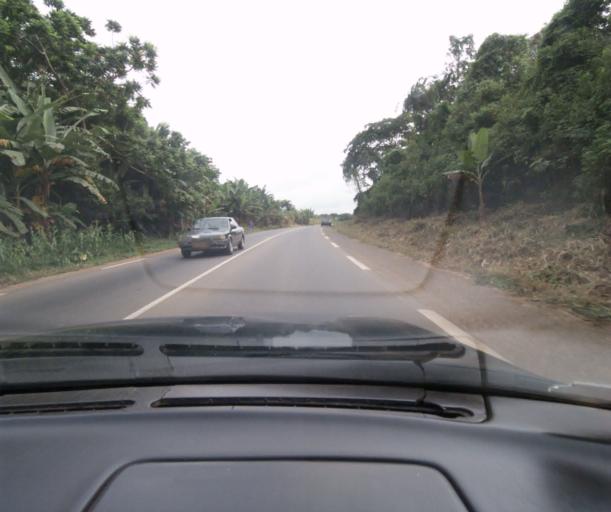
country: CM
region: Centre
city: Obala
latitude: 4.0970
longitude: 11.5379
